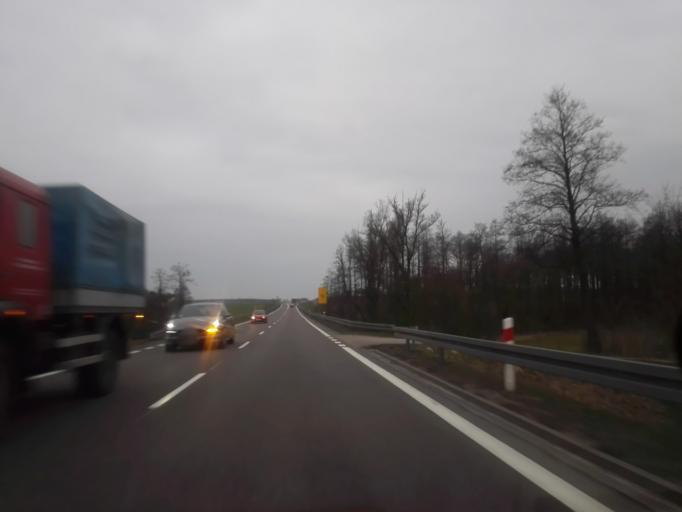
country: PL
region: Podlasie
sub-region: Powiat grajewski
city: Szczuczyn
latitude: 53.5035
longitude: 22.2352
